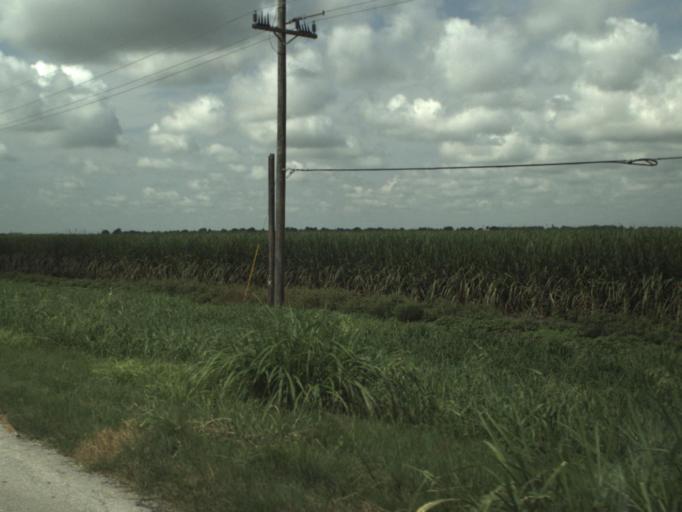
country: US
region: Florida
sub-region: Palm Beach County
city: Belle Glade
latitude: 26.7234
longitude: -80.6841
